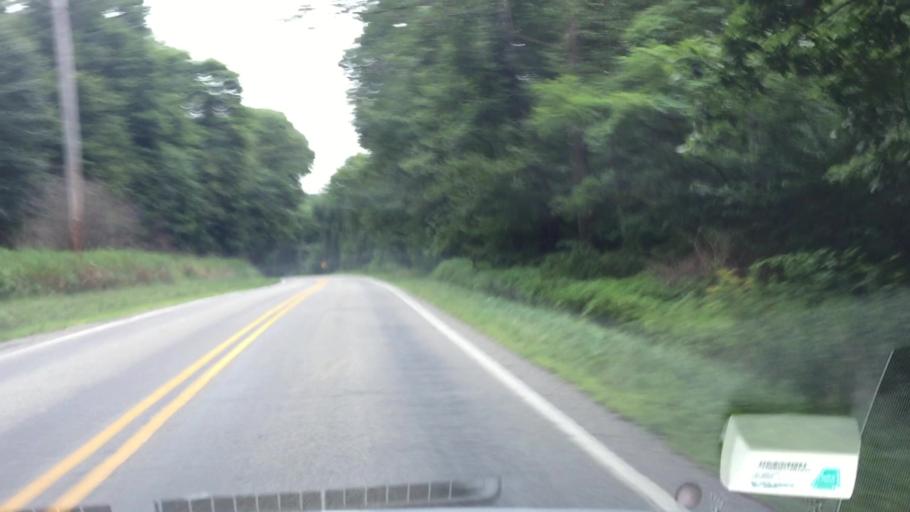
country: US
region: Pennsylvania
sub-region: Allegheny County
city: Curtisville
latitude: 40.7029
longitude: -79.8472
